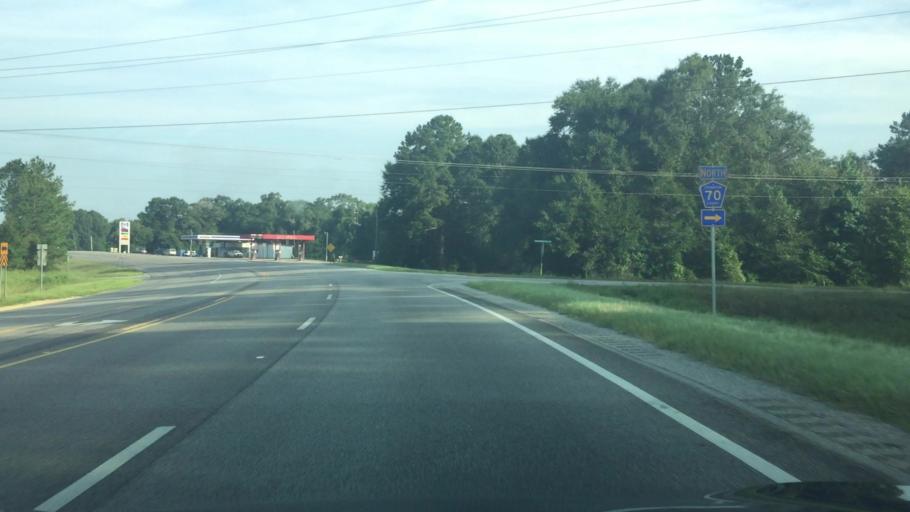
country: US
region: Alabama
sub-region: Covington County
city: Andalusia
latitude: 31.3460
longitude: -86.5255
